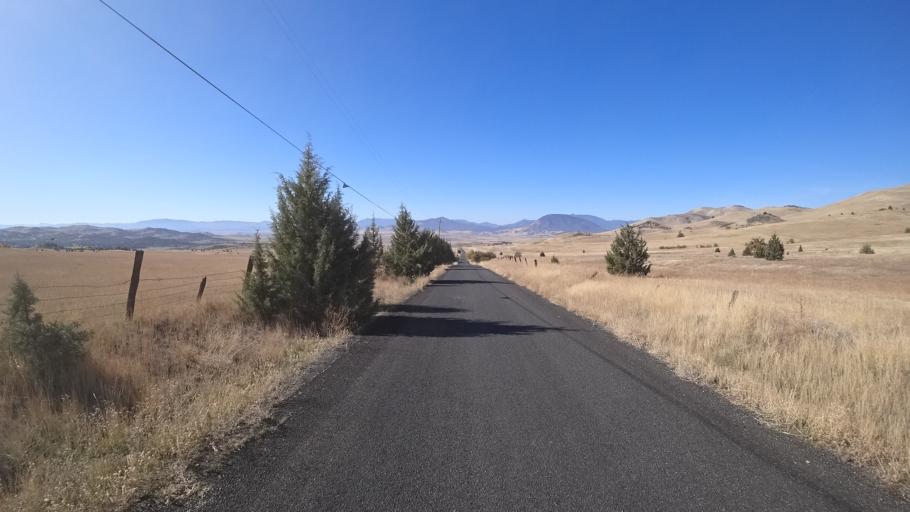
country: US
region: California
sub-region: Siskiyou County
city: Montague
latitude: 41.8305
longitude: -122.3447
